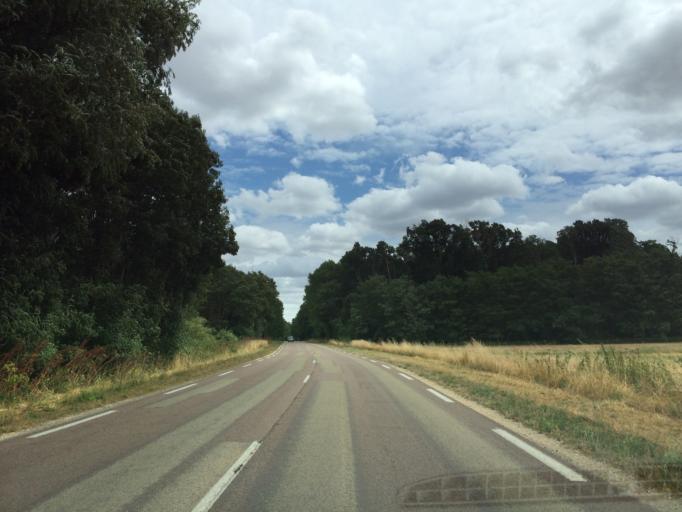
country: FR
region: Bourgogne
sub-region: Departement de l'Yonne
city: Fleury-la-Vallee
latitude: 47.8384
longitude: 3.4019
